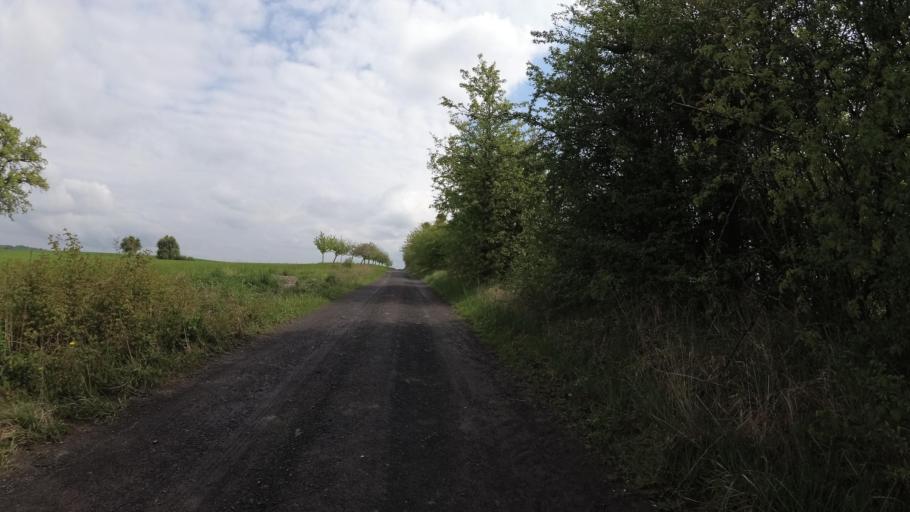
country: DE
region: Saarland
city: Merzig
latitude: 49.4037
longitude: 6.5789
